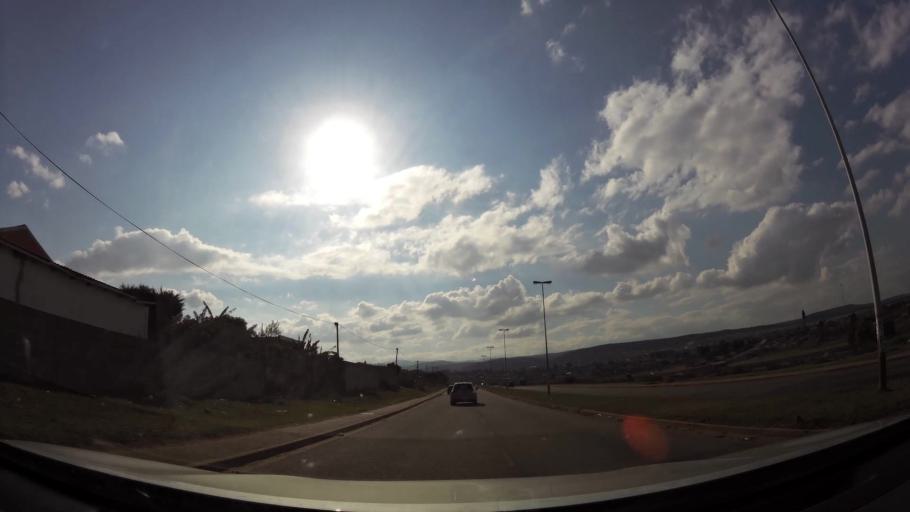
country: ZA
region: Eastern Cape
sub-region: Nelson Mandela Bay Metropolitan Municipality
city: Uitenhage
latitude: -33.7499
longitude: 25.3835
